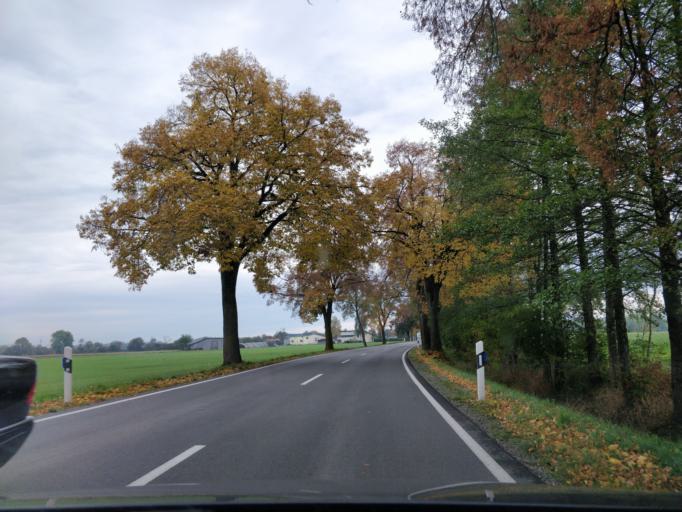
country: DE
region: Bavaria
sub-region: Swabia
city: Wiedergeltingen
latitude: 48.0367
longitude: 10.6819
